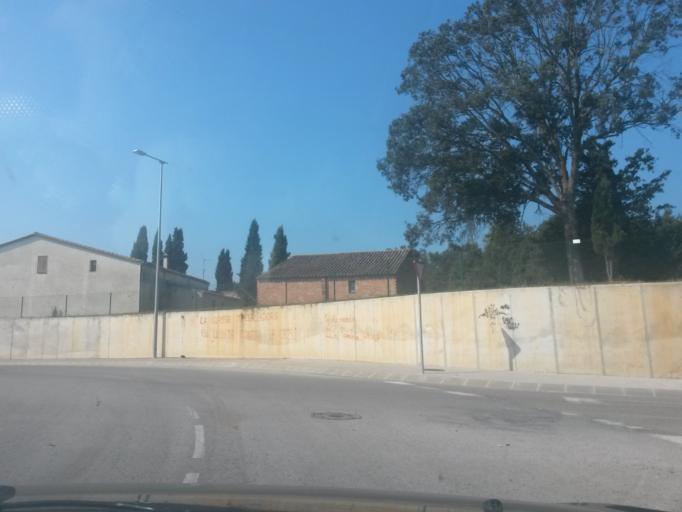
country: ES
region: Catalonia
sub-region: Provincia de Girona
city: Fornells de la Selva
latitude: 41.9432
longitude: 2.8004
